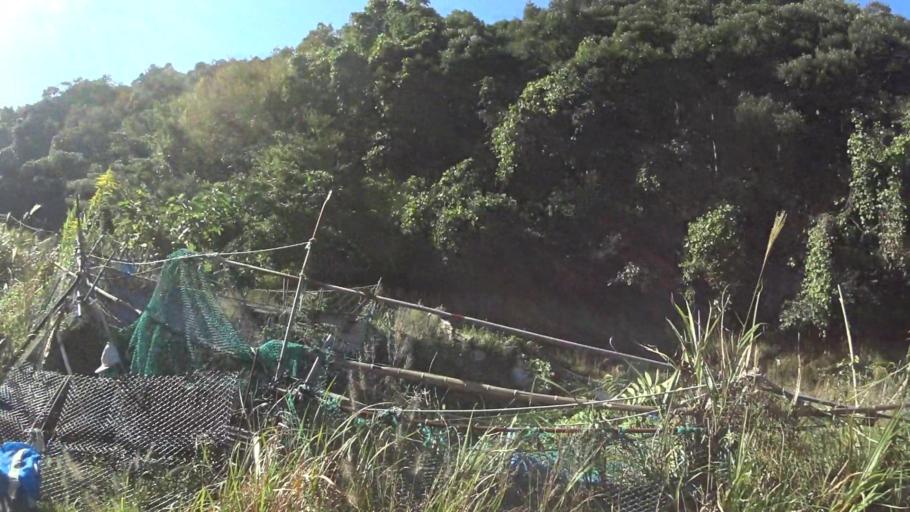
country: JP
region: Hyogo
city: Toyooka
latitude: 35.6465
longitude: 134.8741
